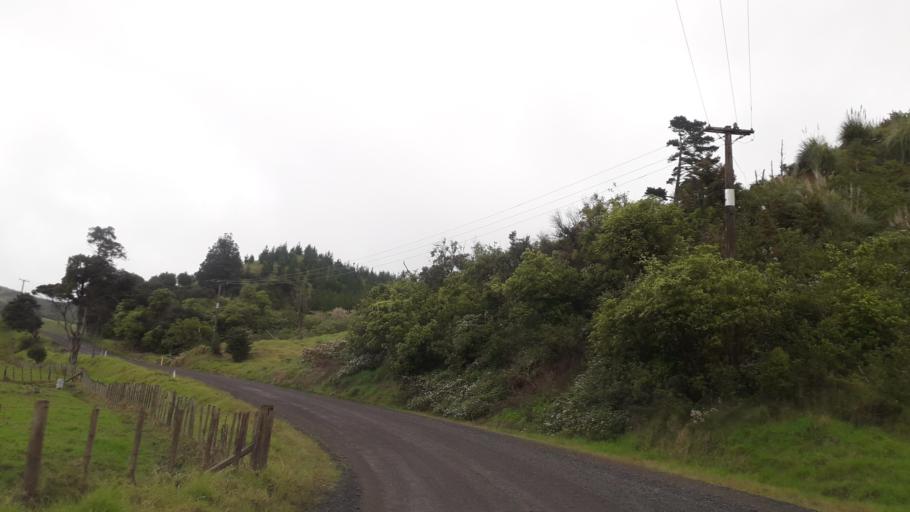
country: NZ
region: Northland
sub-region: Far North District
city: Ahipara
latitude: -35.4312
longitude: 173.3477
